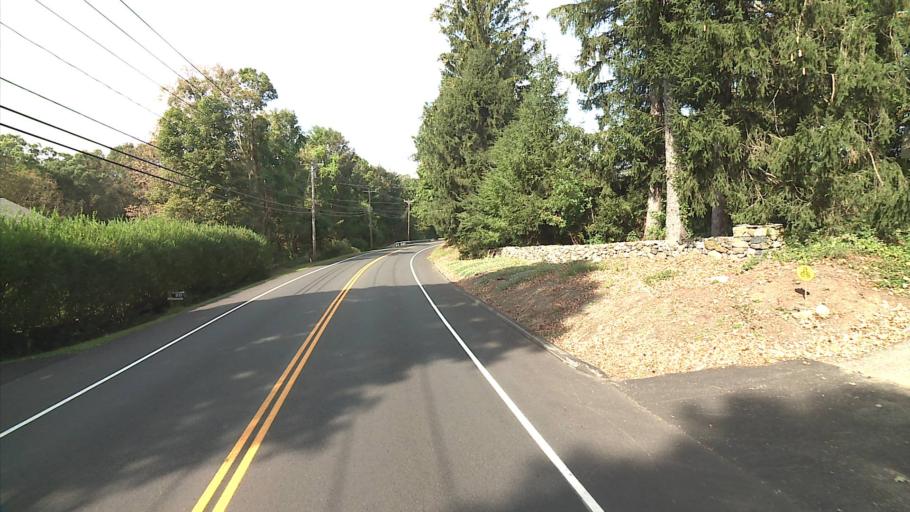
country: US
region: Connecticut
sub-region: Fairfield County
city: Newtown
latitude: 41.3925
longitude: -73.2266
